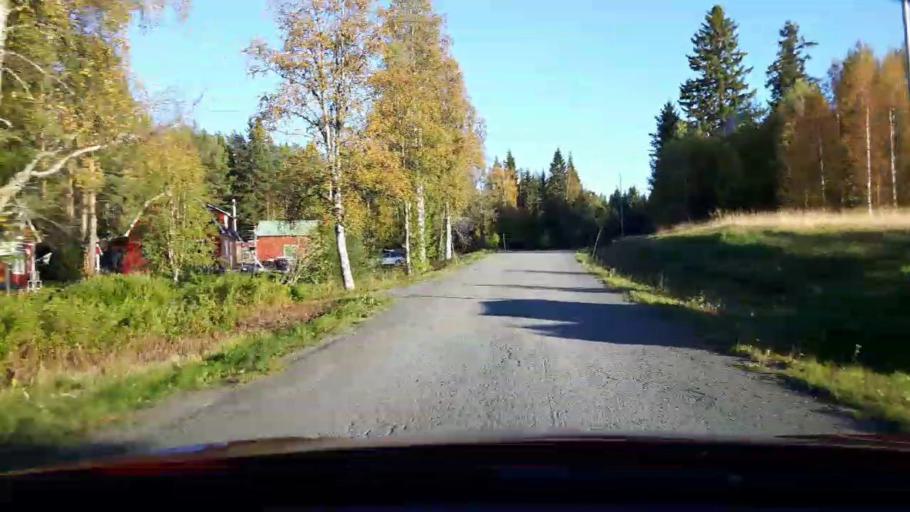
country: SE
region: Jaemtland
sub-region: OEstersunds Kommun
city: Lit
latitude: 63.6089
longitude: 14.7796
